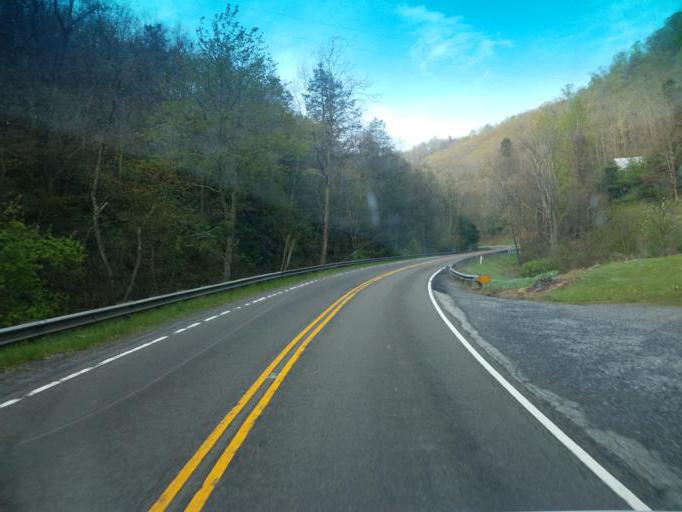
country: US
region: Virginia
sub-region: Smyth County
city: Atkins
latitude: 36.8042
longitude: -81.4037
